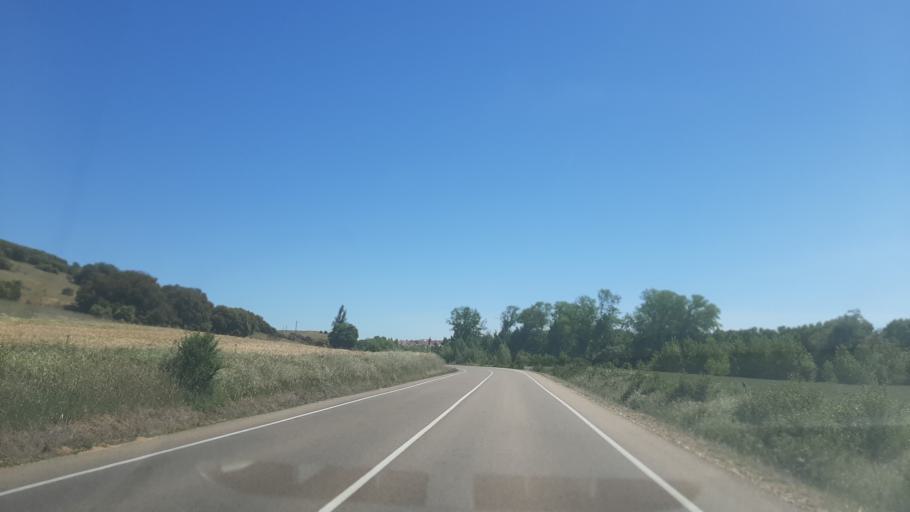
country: ES
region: Castille and Leon
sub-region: Provincia de Salamanca
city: Alba de Tormes
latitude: 40.8146
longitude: -5.5279
